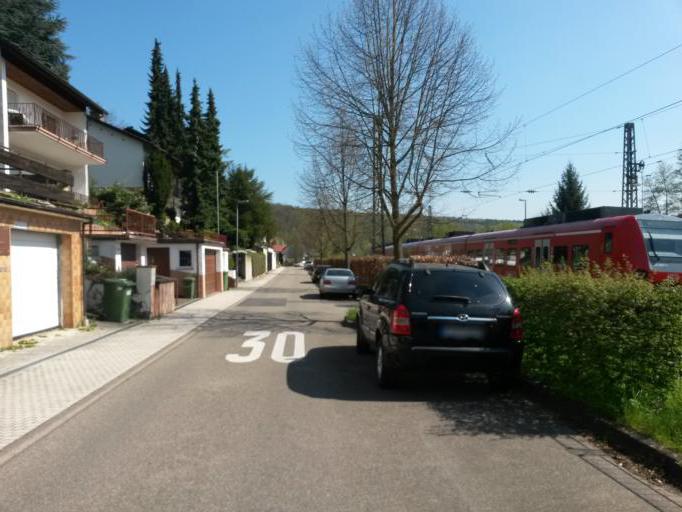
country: DE
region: Baden-Wuerttemberg
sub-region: Karlsruhe Region
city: Joehlingen
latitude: 48.9849
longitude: 8.5485
